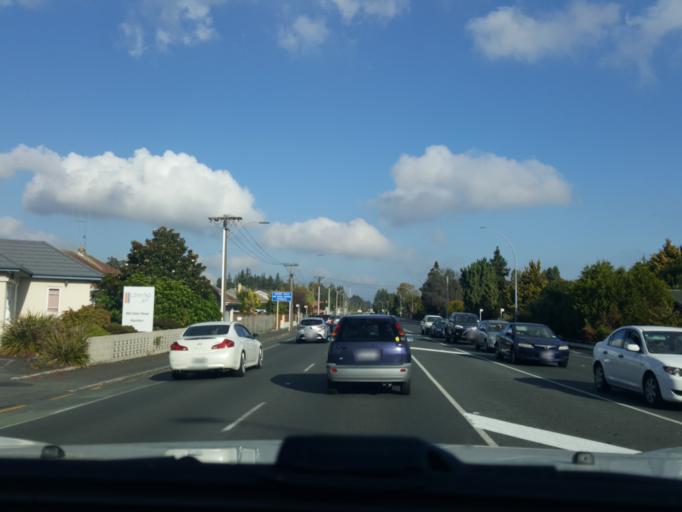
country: NZ
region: Waikato
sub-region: Hamilton City
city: Hamilton
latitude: -37.7699
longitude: 175.2628
